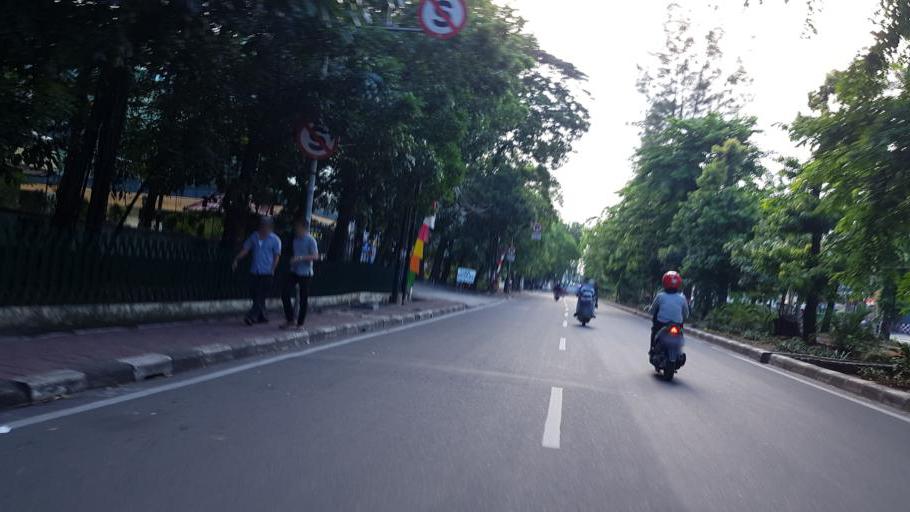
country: ID
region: Jakarta Raya
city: Jakarta
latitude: -6.1374
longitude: 106.7927
